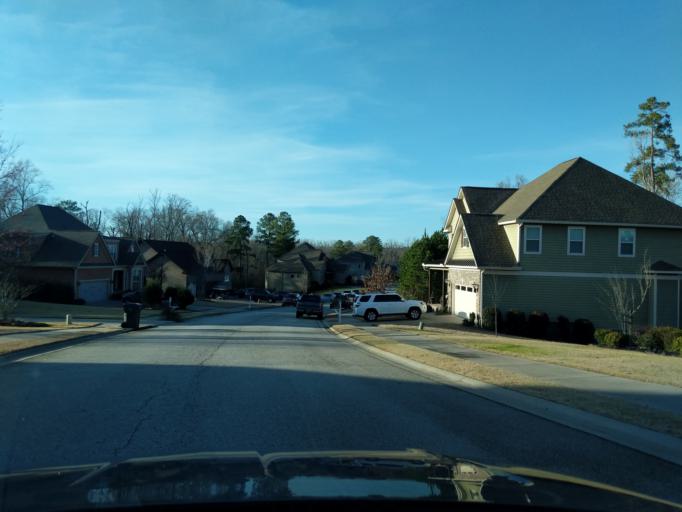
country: US
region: Georgia
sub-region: Columbia County
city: Evans
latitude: 33.5890
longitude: -82.2009
